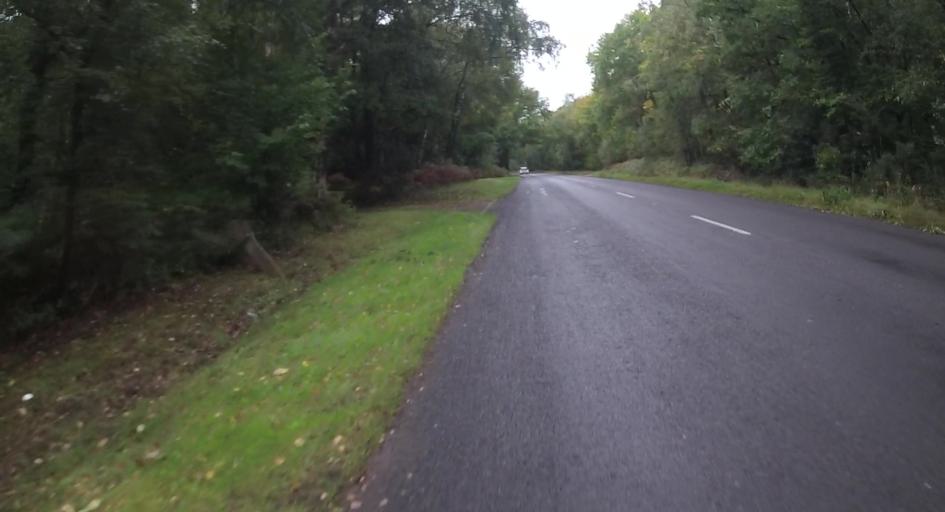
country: GB
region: England
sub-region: West Berkshire
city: Thatcham
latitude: 51.4220
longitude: -1.1885
